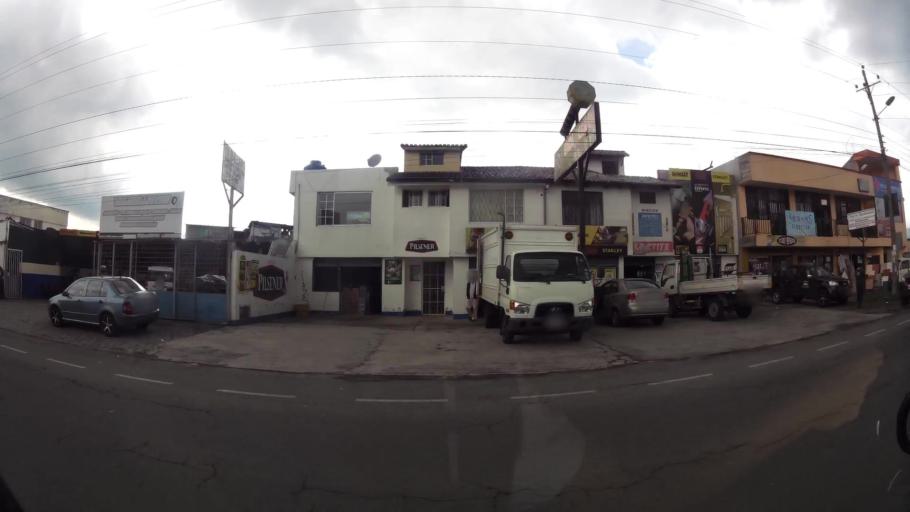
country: EC
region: Pichincha
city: Sangolqui
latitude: -0.3392
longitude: -78.4460
